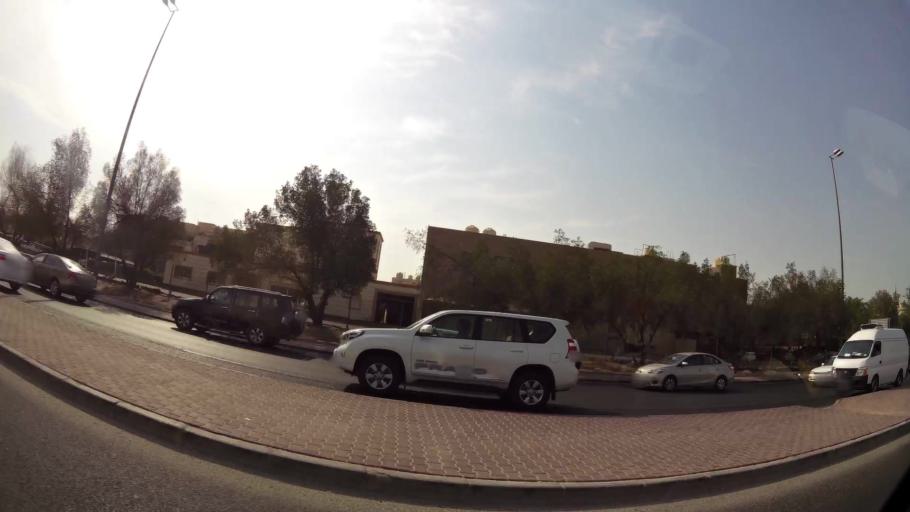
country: KW
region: Al Farwaniyah
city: Janub as Surrah
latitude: 29.2993
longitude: 47.9803
